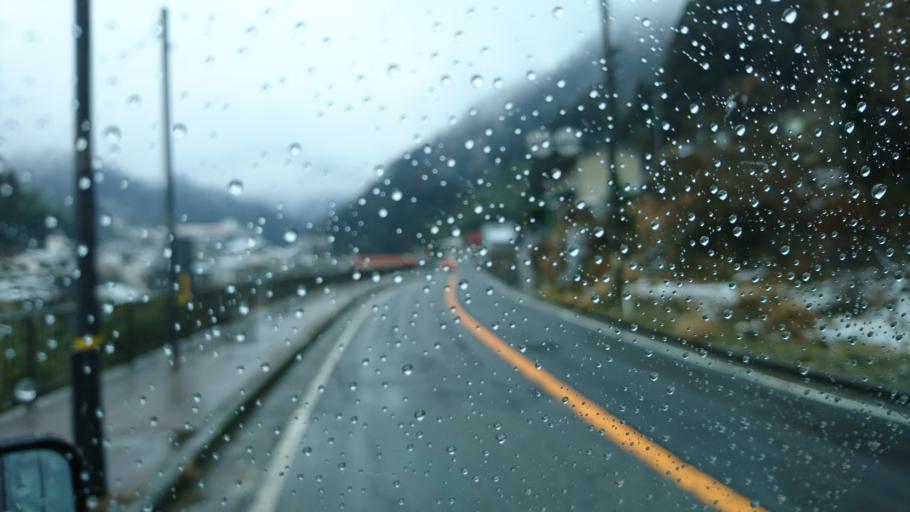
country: JP
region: Tottori
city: Tottori
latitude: 35.5587
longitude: 134.4869
